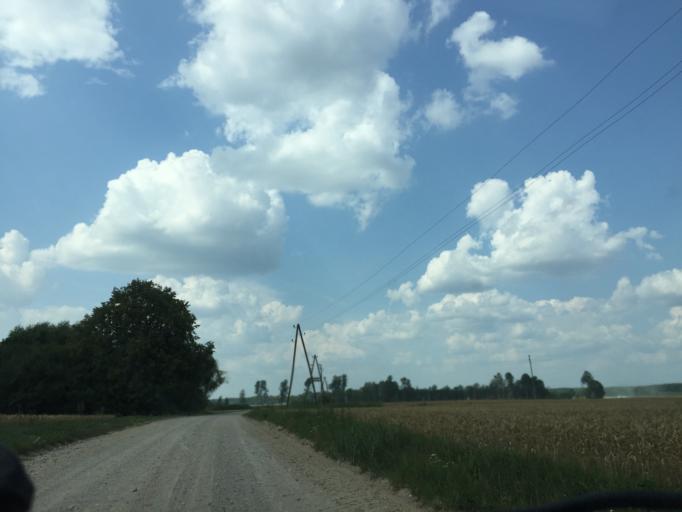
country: LT
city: Zagare
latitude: 56.3452
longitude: 23.1434
